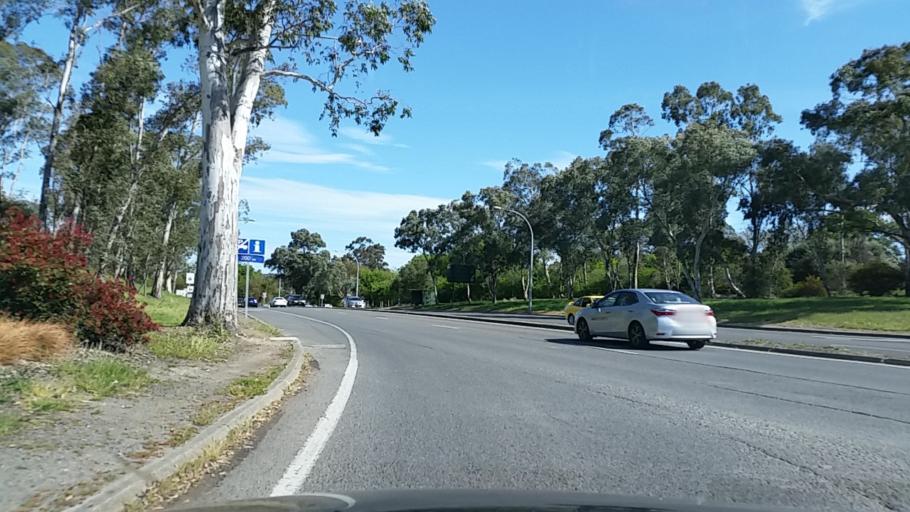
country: AU
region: South Australia
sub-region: Mount Barker
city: Little Hampton
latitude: -35.0595
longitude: 138.8525
